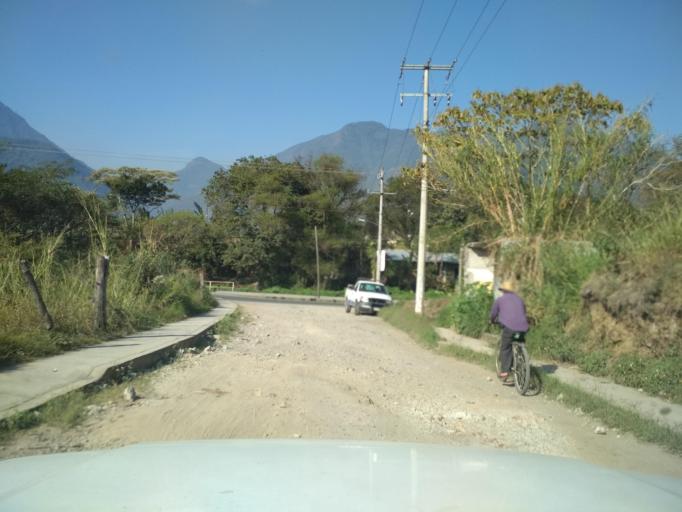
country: MX
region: Veracruz
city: Jalapilla
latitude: 18.8171
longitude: -97.0763
